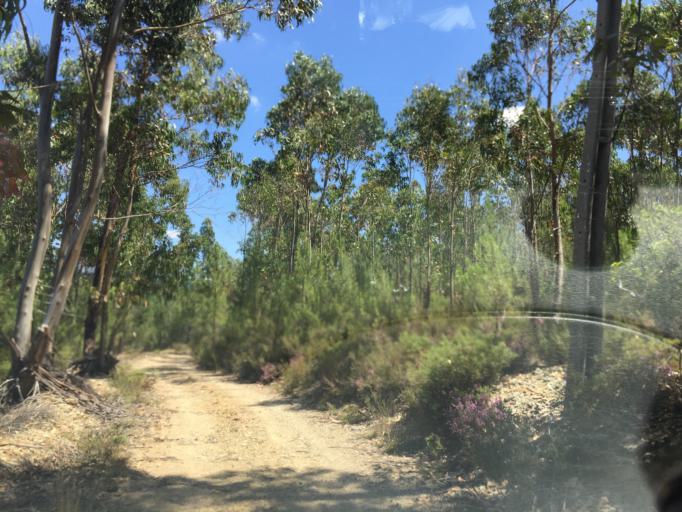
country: PT
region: Coimbra
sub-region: Pampilhosa da Serra
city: Pampilhosa da Serra
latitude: 40.1009
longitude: -7.8461
